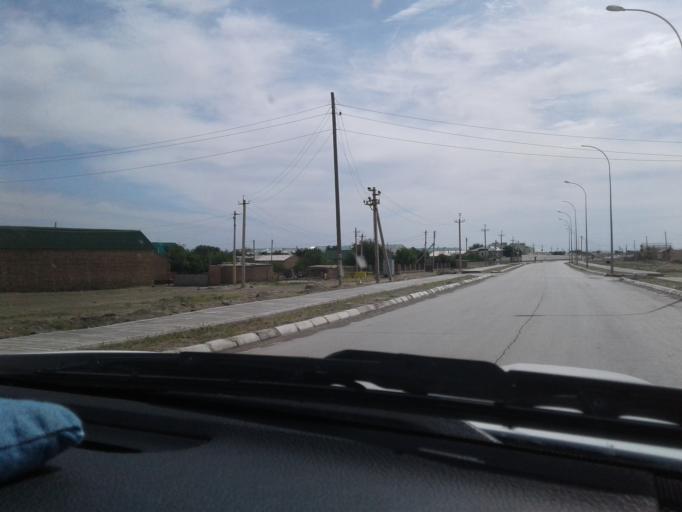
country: TM
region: Balkan
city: Gazanjyk
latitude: 39.2451
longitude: 55.4880
